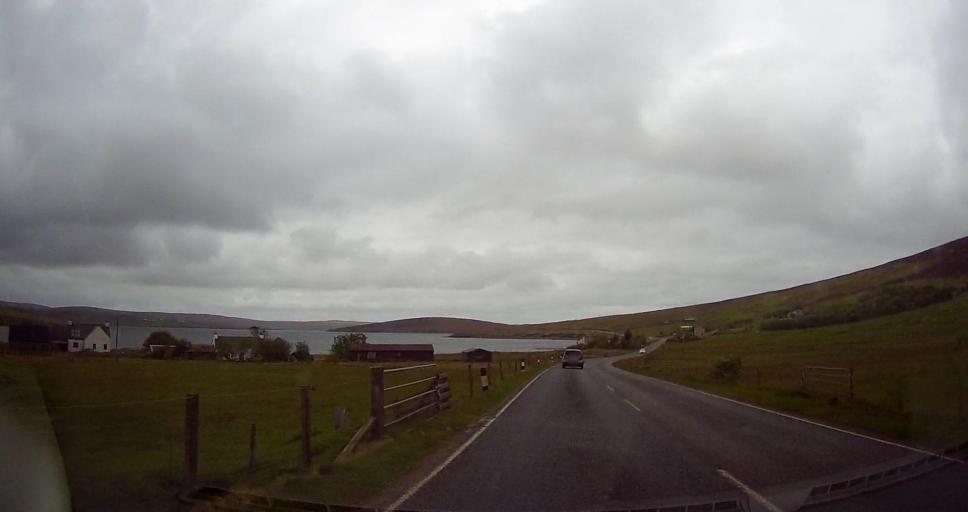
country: GB
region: Scotland
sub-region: Shetland Islands
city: Lerwick
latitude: 60.2431
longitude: -1.3487
